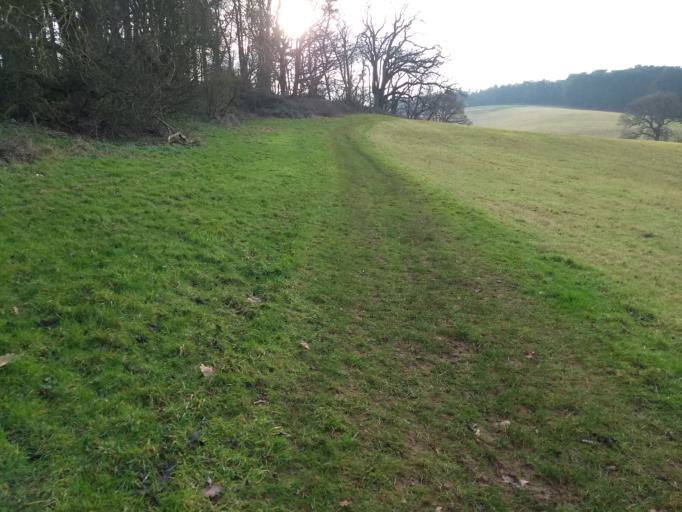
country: GB
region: England
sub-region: Central Bedfordshire
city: Woburn
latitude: 51.9896
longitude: -0.6336
